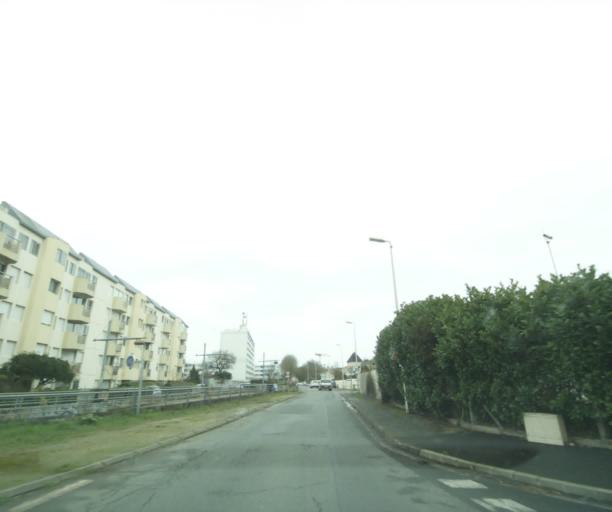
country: FR
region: Poitou-Charentes
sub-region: Departement de la Charente-Maritime
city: Puilboreau
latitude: 46.1734
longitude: -1.1231
